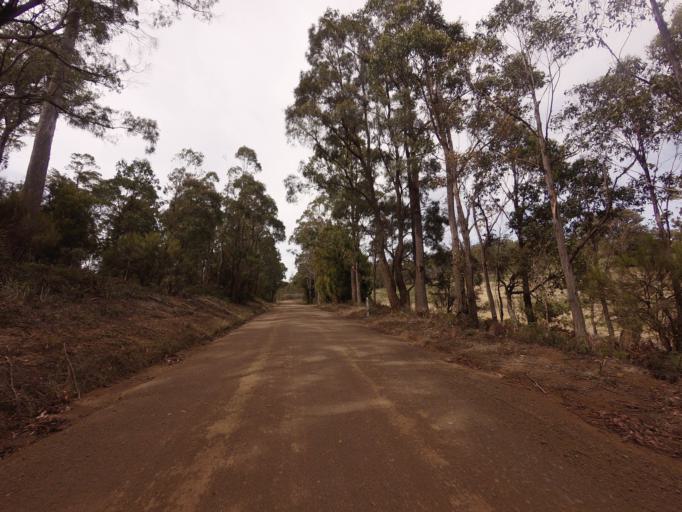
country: AU
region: Tasmania
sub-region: Sorell
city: Sorell
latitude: -42.4843
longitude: 147.6166
